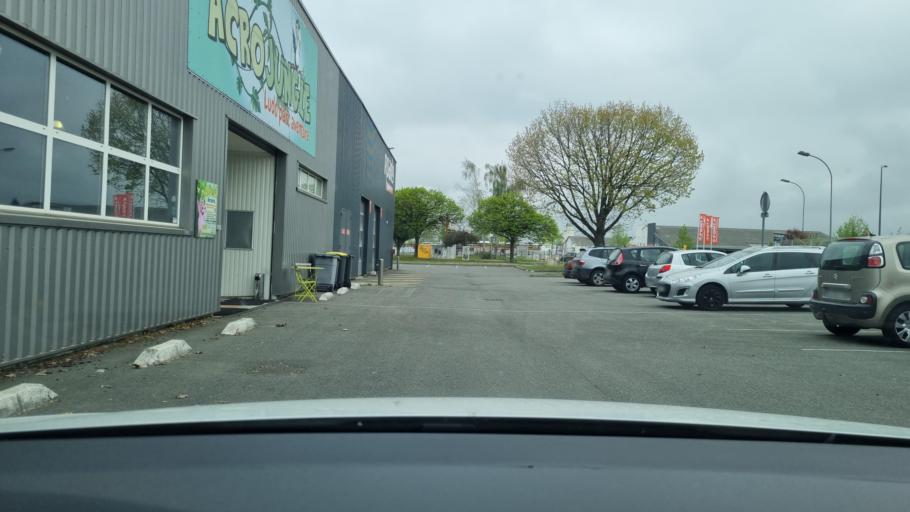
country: FR
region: Aquitaine
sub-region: Departement des Pyrenees-Atlantiques
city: Montardon
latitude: 43.3595
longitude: -0.3840
